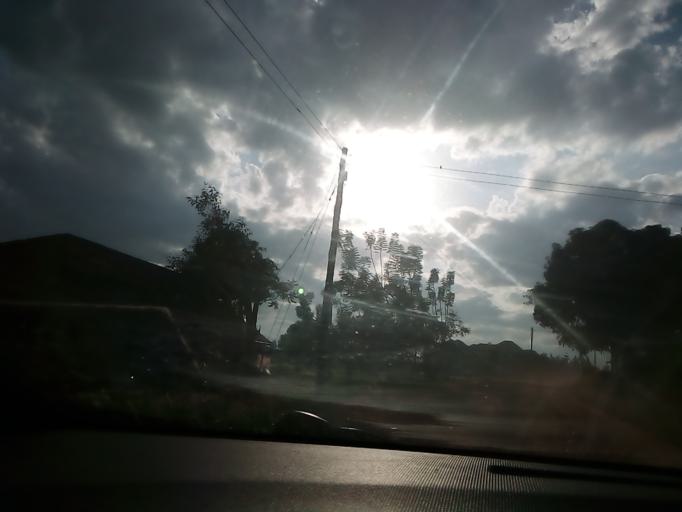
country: UG
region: Central Region
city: Masaka
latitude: -0.3472
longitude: 31.7138
